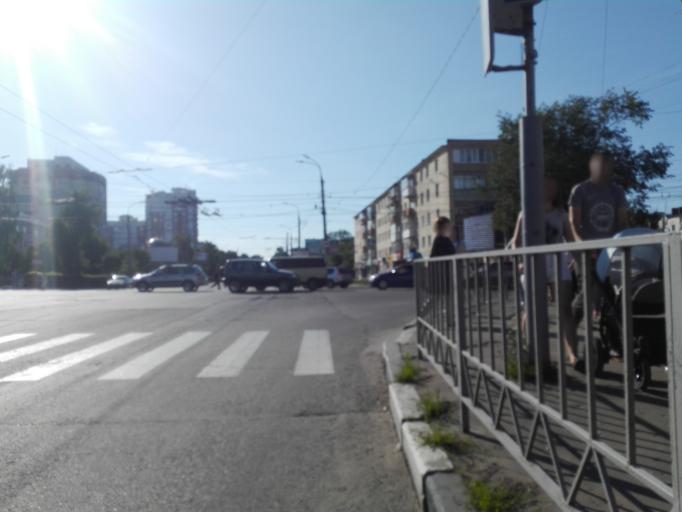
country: RU
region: Orjol
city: Orel
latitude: 52.9793
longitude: 36.0763
